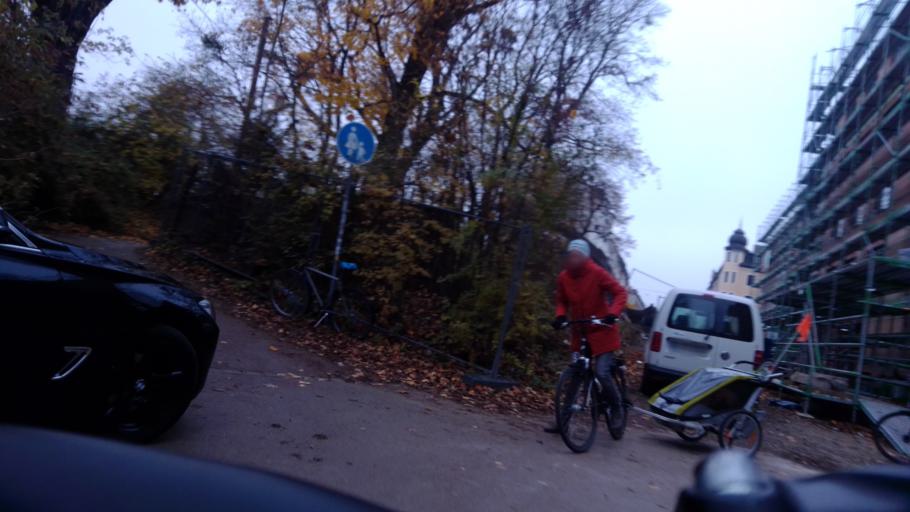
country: DE
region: Bavaria
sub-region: Upper Bavaria
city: Munich
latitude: 48.1074
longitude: 11.5371
